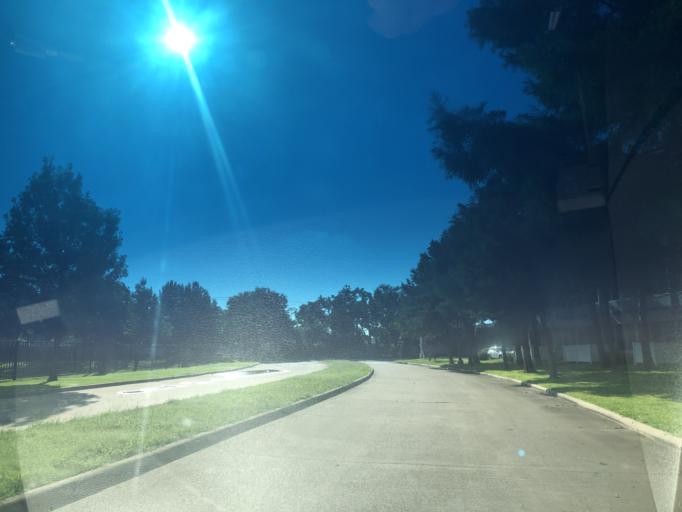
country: US
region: Texas
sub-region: Dallas County
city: Grand Prairie
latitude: 32.7116
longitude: -97.0035
